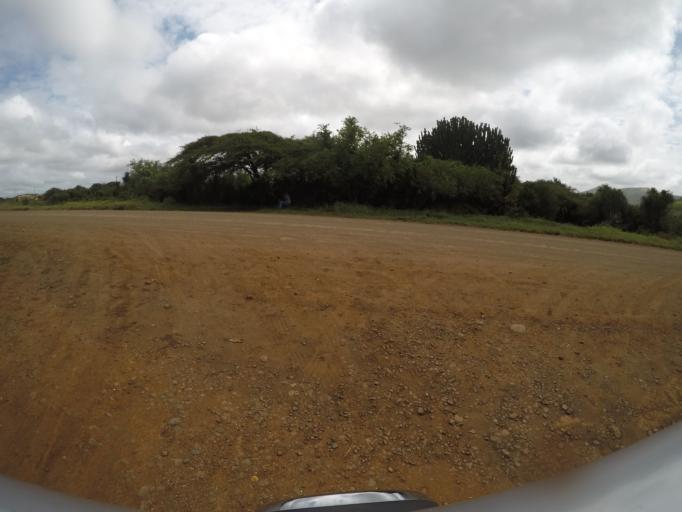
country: ZA
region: KwaZulu-Natal
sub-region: uThungulu District Municipality
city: Empangeni
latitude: -28.6038
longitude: 31.8460
